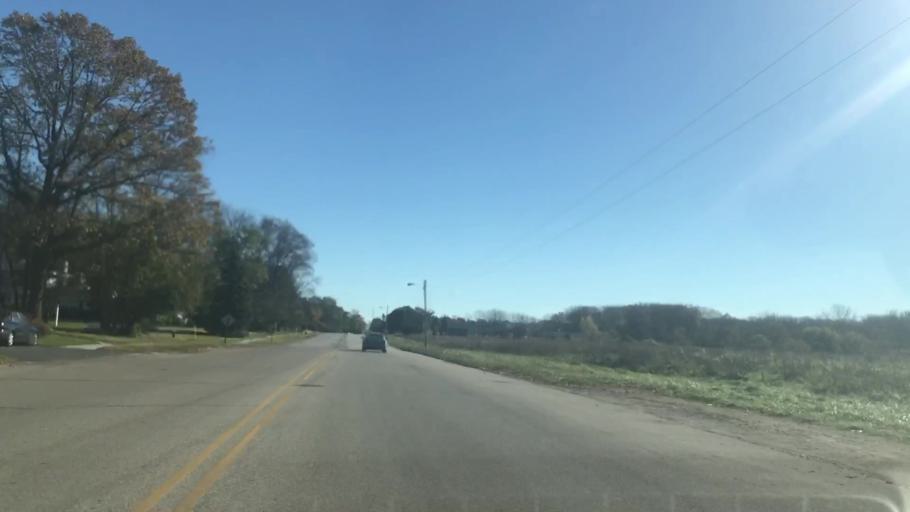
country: US
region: Wisconsin
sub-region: Waukesha County
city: Menomonee Falls
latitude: 43.1702
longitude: -88.1319
